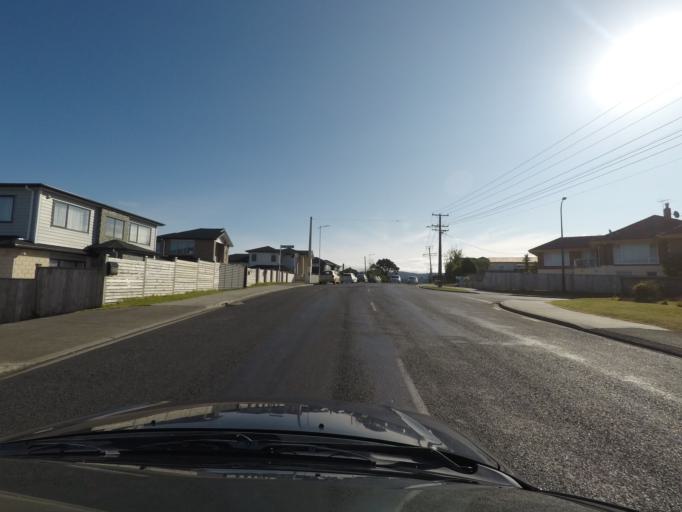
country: NZ
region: Auckland
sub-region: Auckland
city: Rosebank
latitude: -36.8735
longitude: 174.5997
